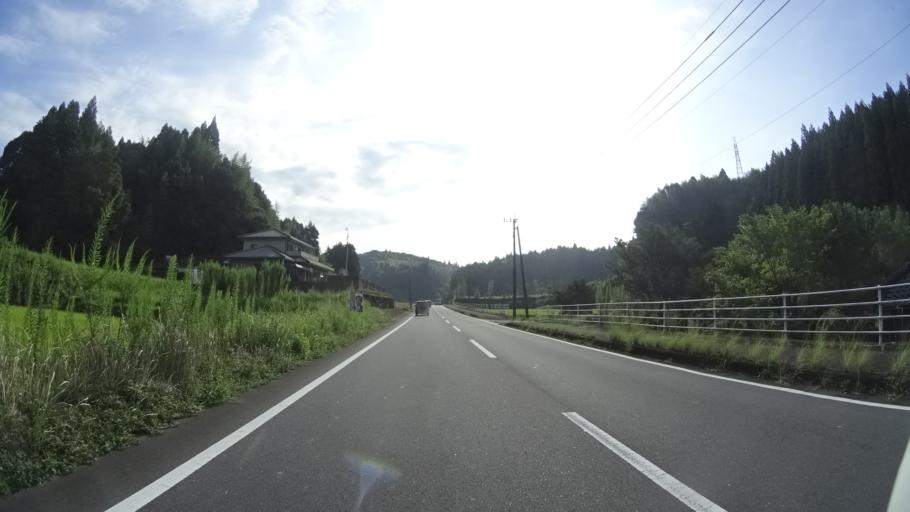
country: JP
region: Kagoshima
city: Okuchi-shinohara
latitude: 32.0181
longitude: 130.6230
